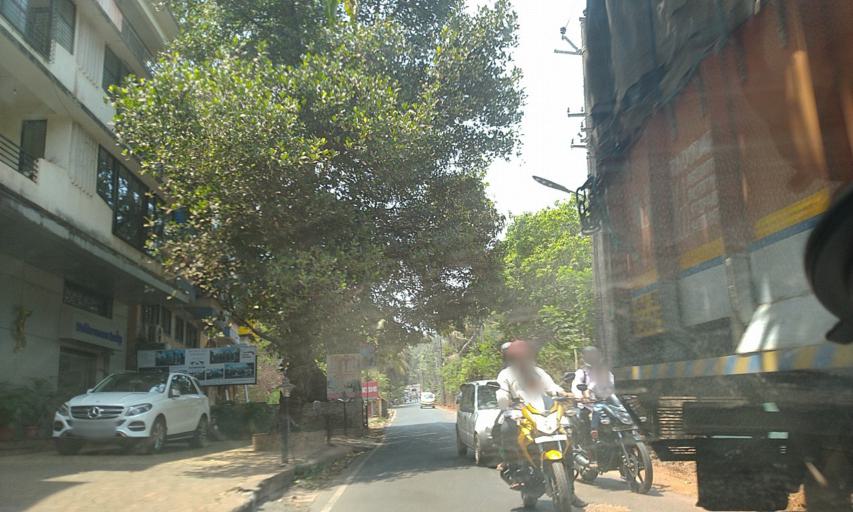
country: IN
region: Goa
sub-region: North Goa
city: Mapuca
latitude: 15.5939
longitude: 73.8026
